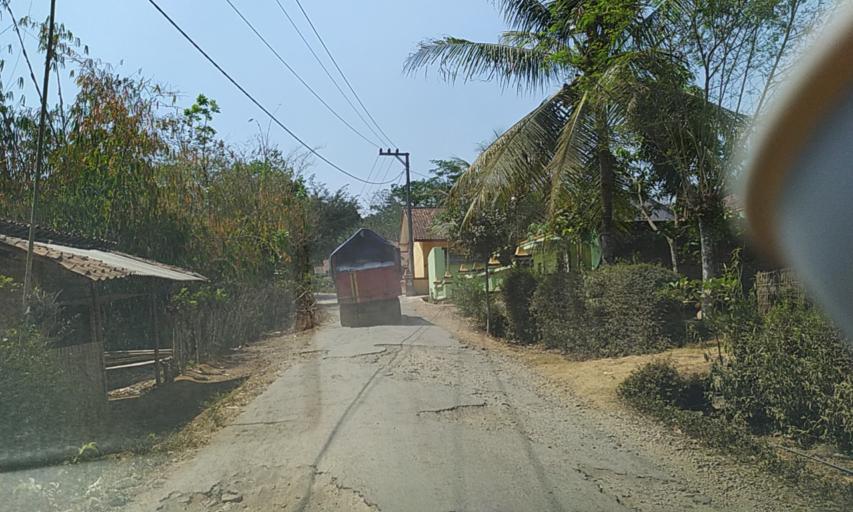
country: ID
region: Central Java
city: Karanggintung
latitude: -7.4568
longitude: 108.8564
